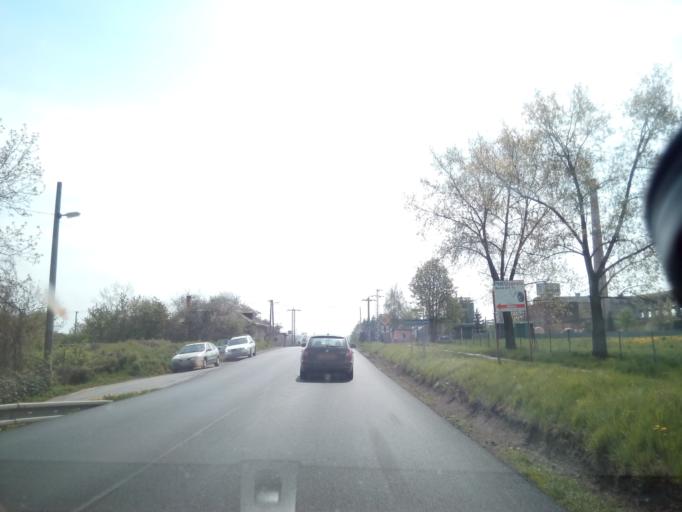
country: SK
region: Presovsky
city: Giraltovce
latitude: 49.0060
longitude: 21.5424
